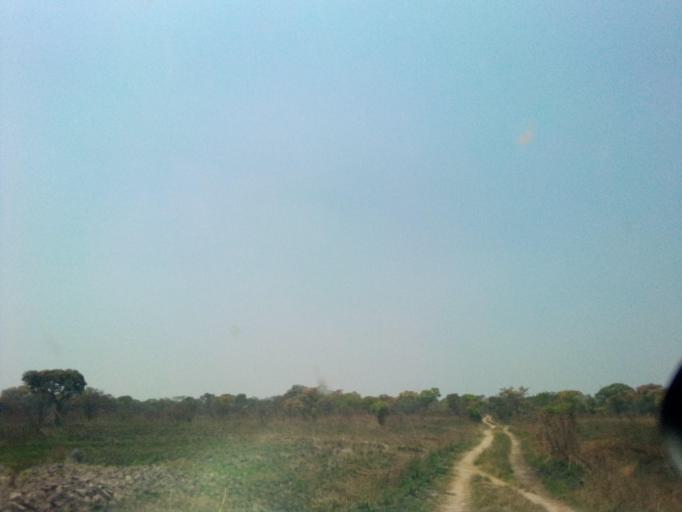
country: ZM
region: Copperbelt
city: Kataba
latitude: -12.2468
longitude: 30.3953
